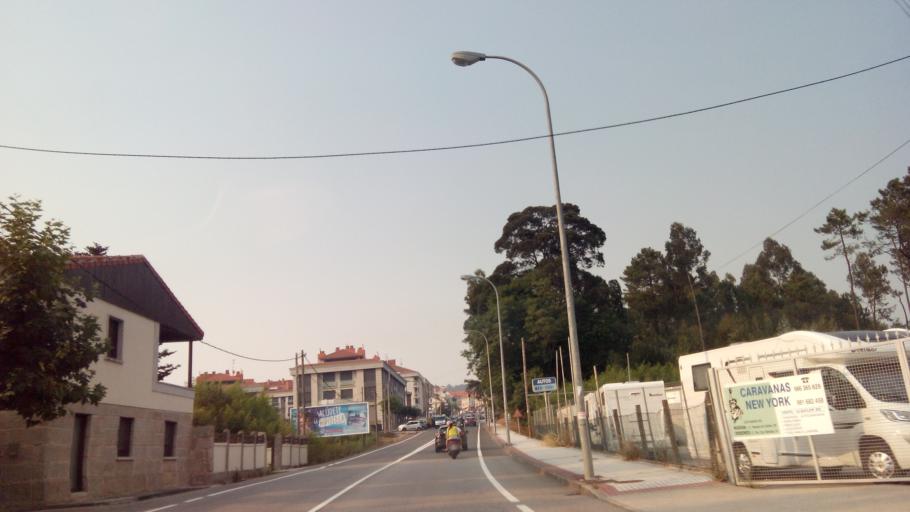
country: ES
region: Galicia
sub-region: Provincia de Pontevedra
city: Nigran
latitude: 42.1369
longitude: -8.8079
